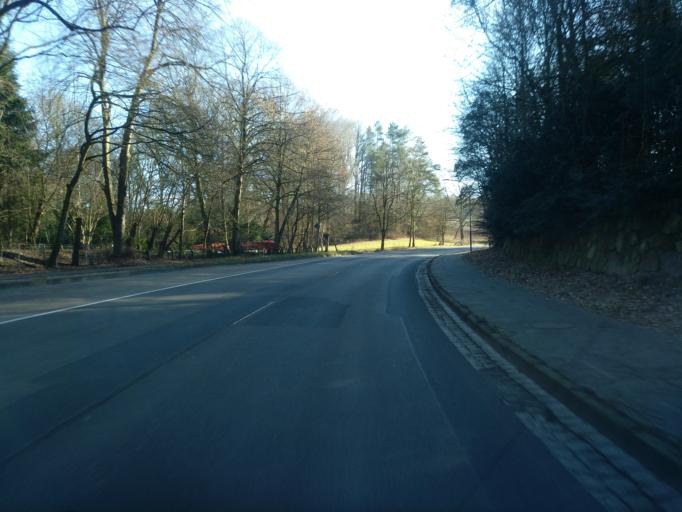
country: DE
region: Hamburg
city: Harburg
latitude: 53.4520
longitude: 9.9053
